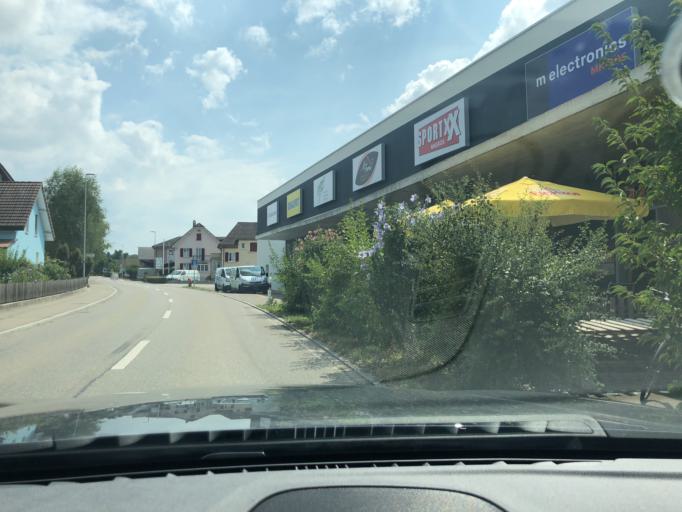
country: CH
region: Aargau
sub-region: Bezirk Bremgarten
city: Bremgarten
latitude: 47.3519
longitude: 8.3502
